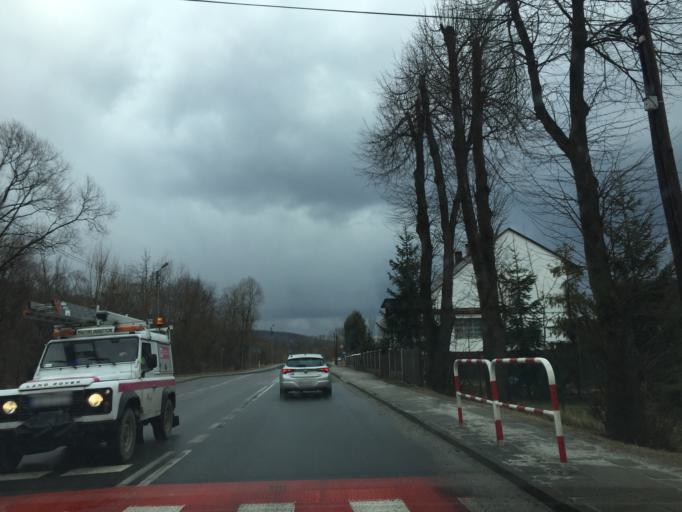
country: PL
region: Lesser Poland Voivodeship
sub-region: Powiat suski
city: Zembrzyce
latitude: 49.7697
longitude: 19.6369
